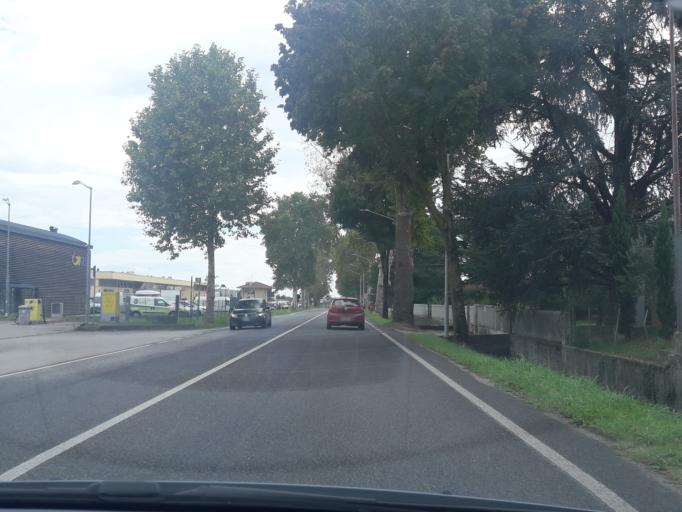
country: IT
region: Friuli Venezia Giulia
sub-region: Provincia di Udine
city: Udine
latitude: 46.0284
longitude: 13.2585
